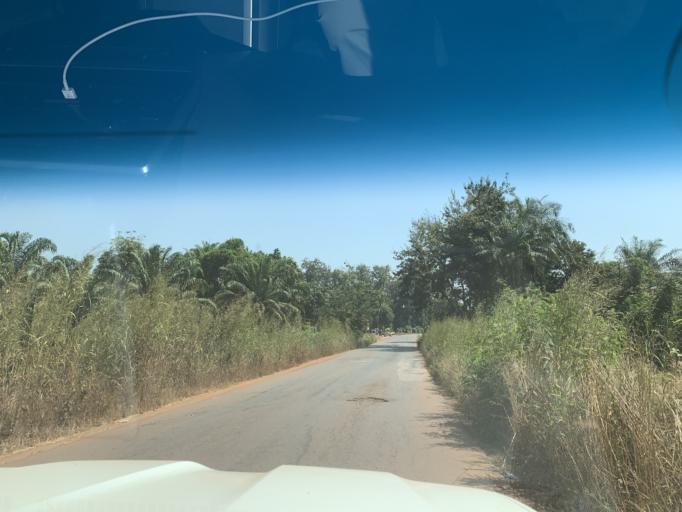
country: GN
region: Kindia
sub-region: Kindia
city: Kindia
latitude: 10.0035
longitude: -12.7678
